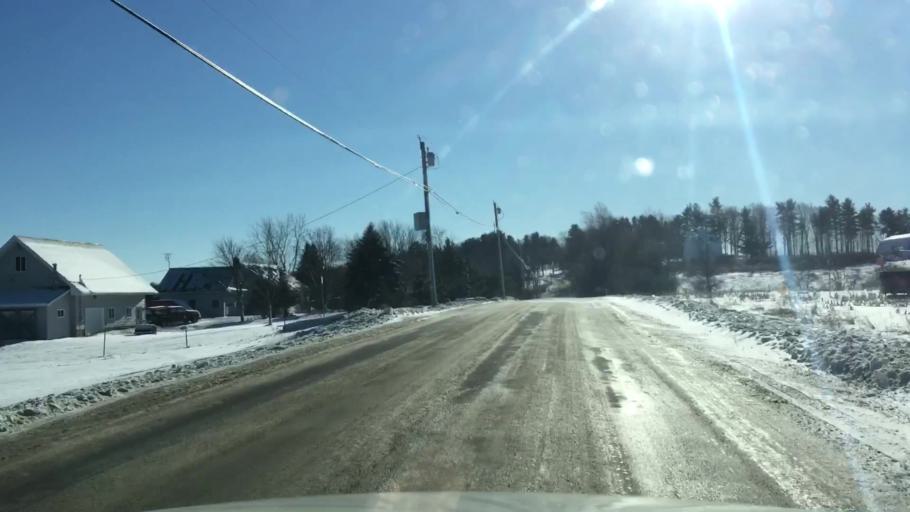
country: US
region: Maine
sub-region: Kennebec County
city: Winthrop
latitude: 44.3431
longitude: -69.9897
